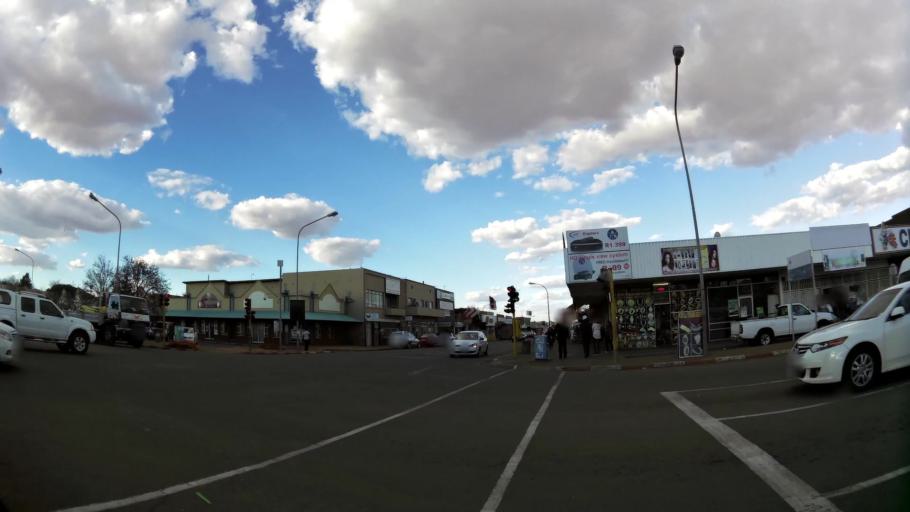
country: ZA
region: North-West
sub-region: Dr Kenneth Kaunda District Municipality
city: Potchefstroom
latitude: -26.7112
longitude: 27.0993
